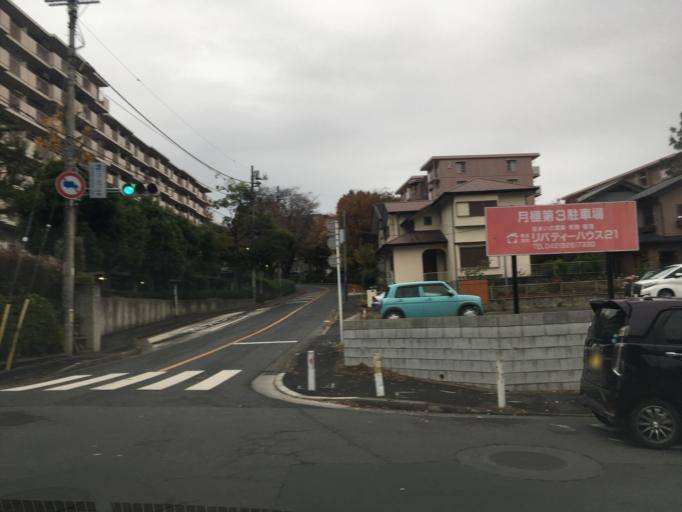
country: JP
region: Saitama
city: Tokorozawa
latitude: 35.7807
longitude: 139.4339
